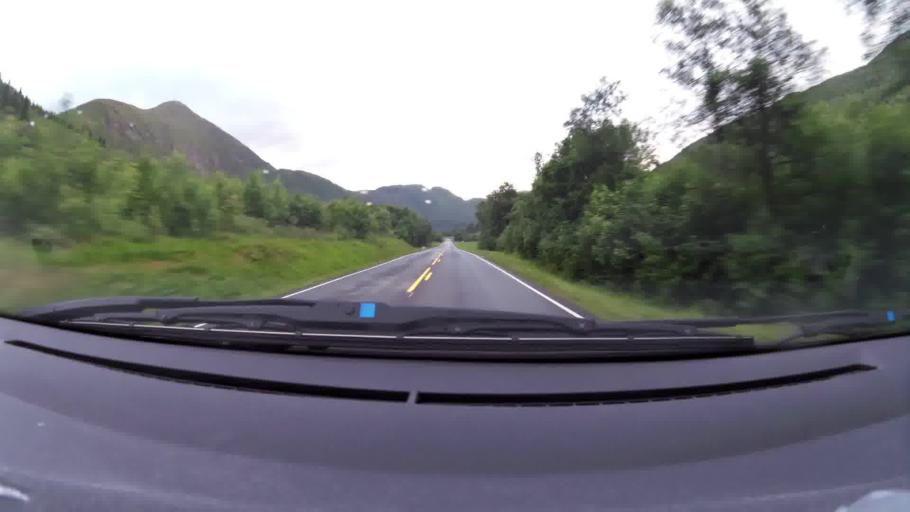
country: NO
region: More og Romsdal
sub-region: Molde
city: Molde
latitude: 62.7956
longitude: 7.2767
